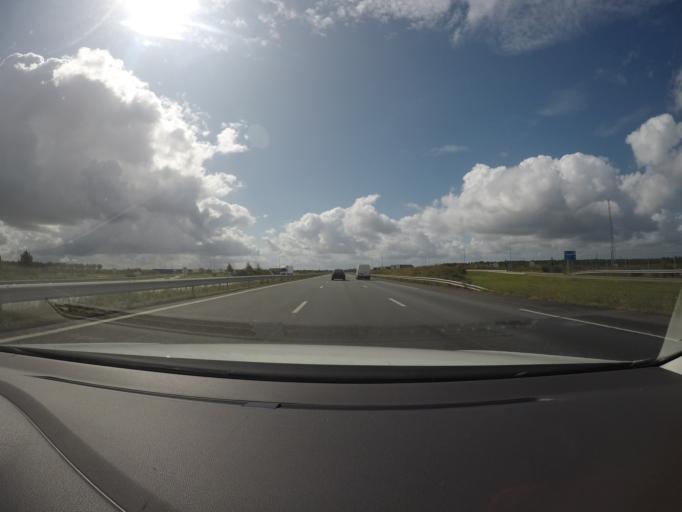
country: FR
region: Aquitaine
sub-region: Departement des Landes
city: Labouheyre
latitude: 44.2553
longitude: -0.9023
